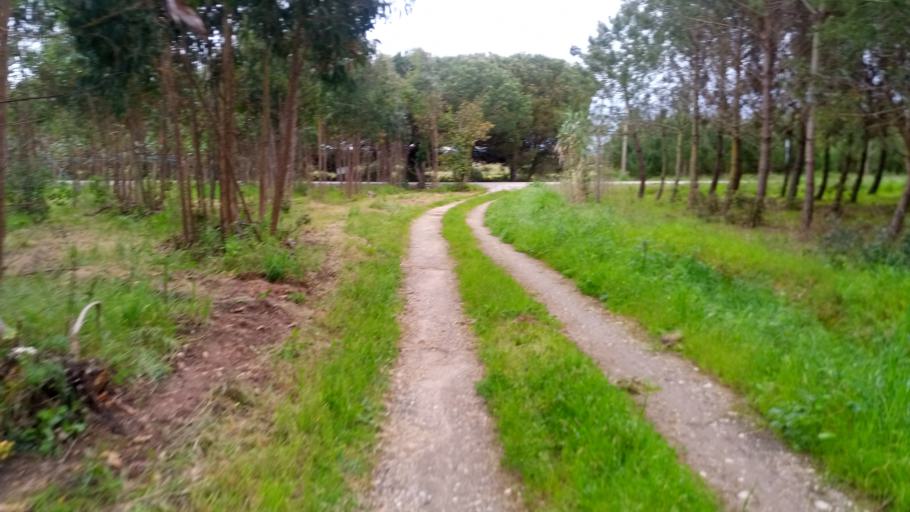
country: PT
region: Leiria
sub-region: Caldas da Rainha
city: Caldas da Rainha
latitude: 39.4487
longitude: -9.1840
